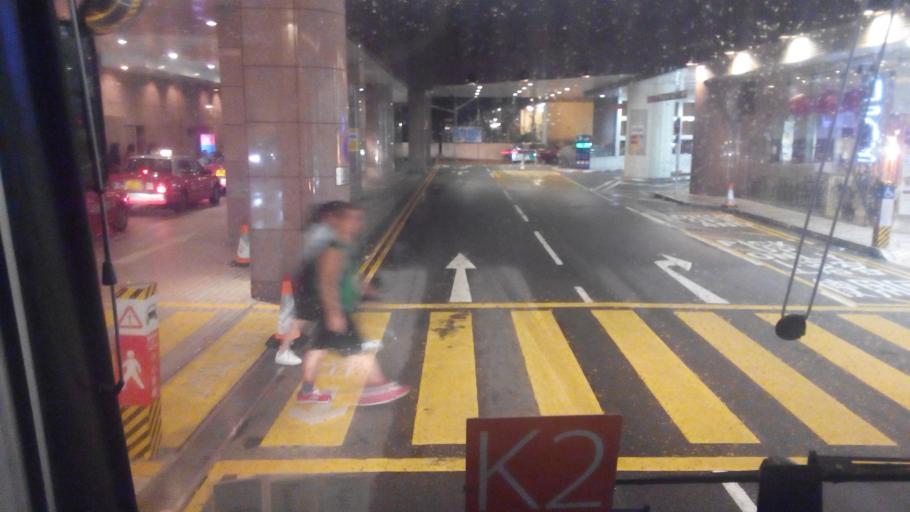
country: HK
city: Hong Kong
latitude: 22.2990
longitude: 114.1679
